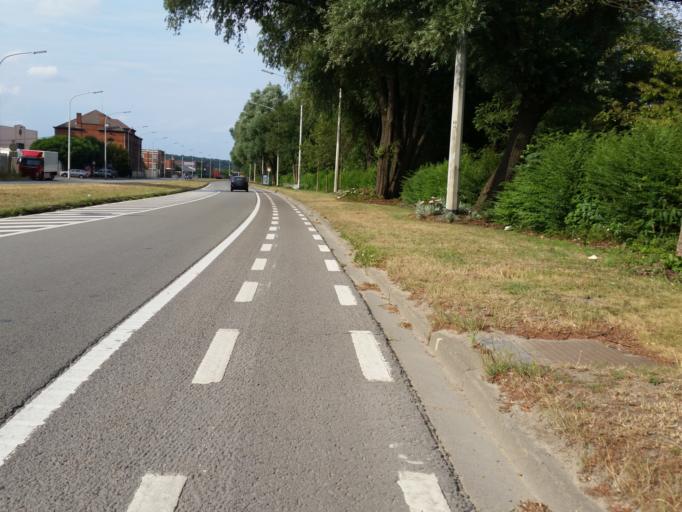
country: BE
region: Flanders
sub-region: Provincie Vlaams-Brabant
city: Diegem
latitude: 50.8941
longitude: 4.4027
